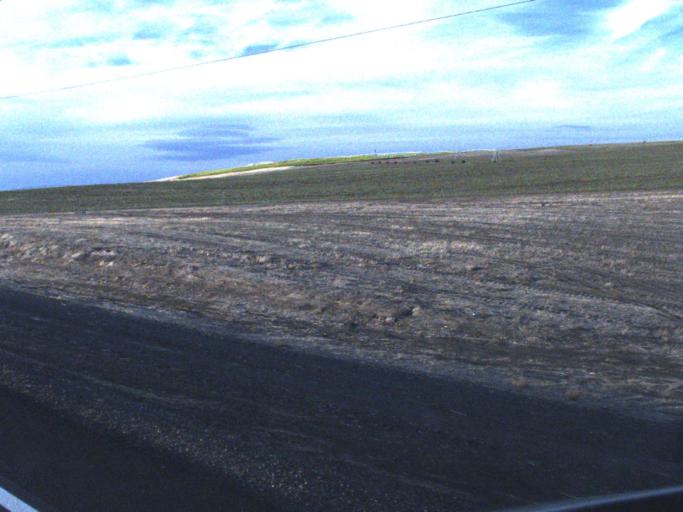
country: US
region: Washington
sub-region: Walla Walla County
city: Burbank
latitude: 46.0613
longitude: -118.7395
